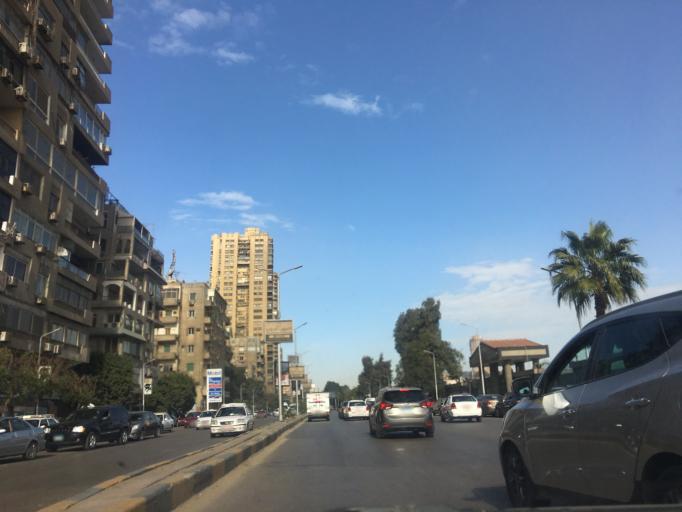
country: EG
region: Al Jizah
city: Al Jizah
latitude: 30.0425
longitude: 31.2194
